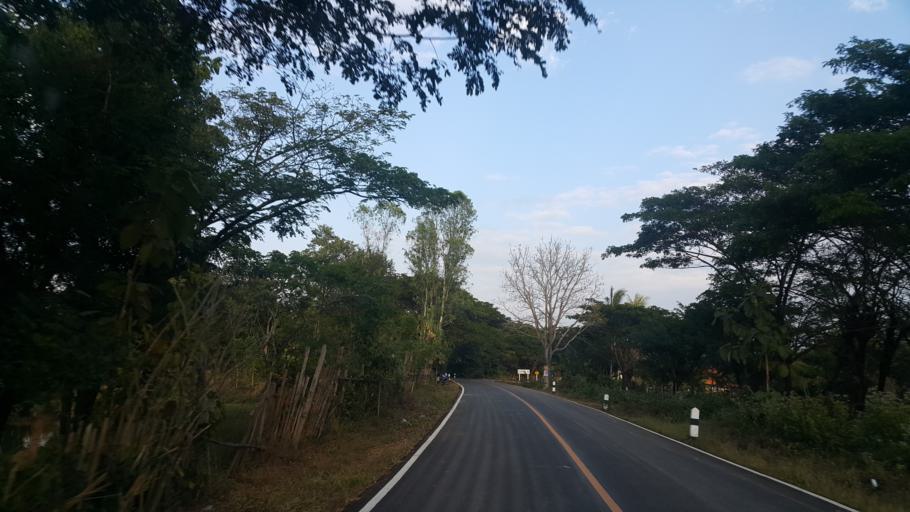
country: TH
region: Lampang
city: Sop Prap
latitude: 17.9425
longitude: 99.3372
